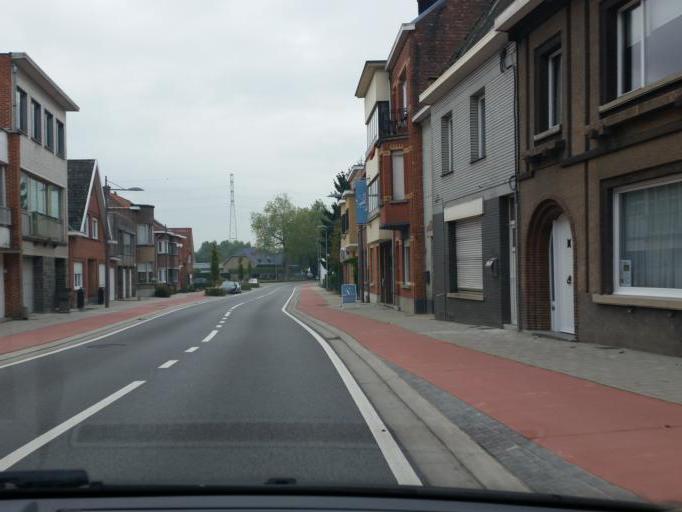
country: BE
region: Flanders
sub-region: Provincie Vlaams-Brabant
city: Steenokkerzeel
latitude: 50.9597
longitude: 4.4974
